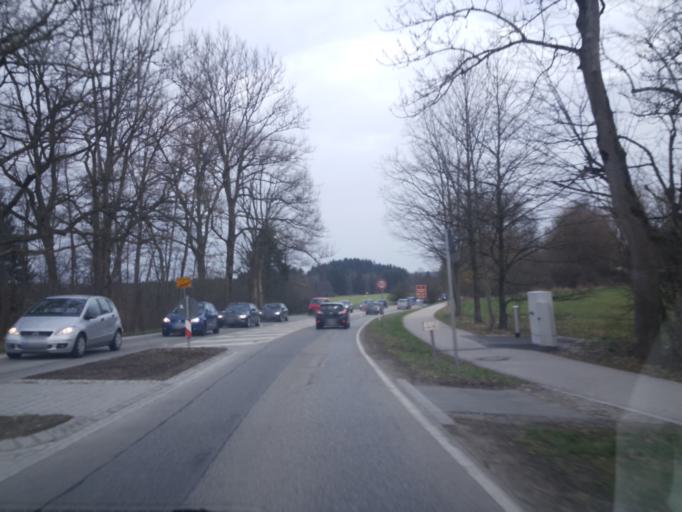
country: DE
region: Bavaria
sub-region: Upper Bavaria
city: Iffeldorf
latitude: 47.7679
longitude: 11.3485
